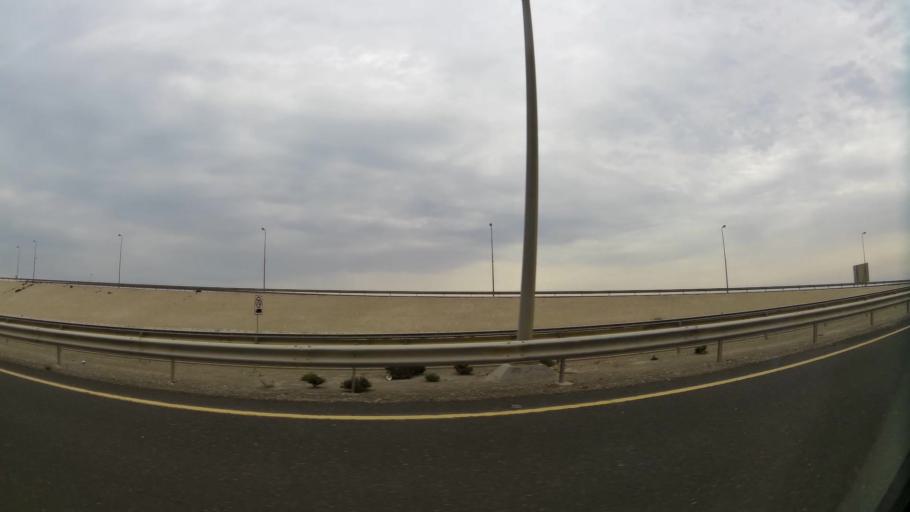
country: BH
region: Central Governorate
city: Dar Kulayb
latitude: 25.8854
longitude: 50.5773
